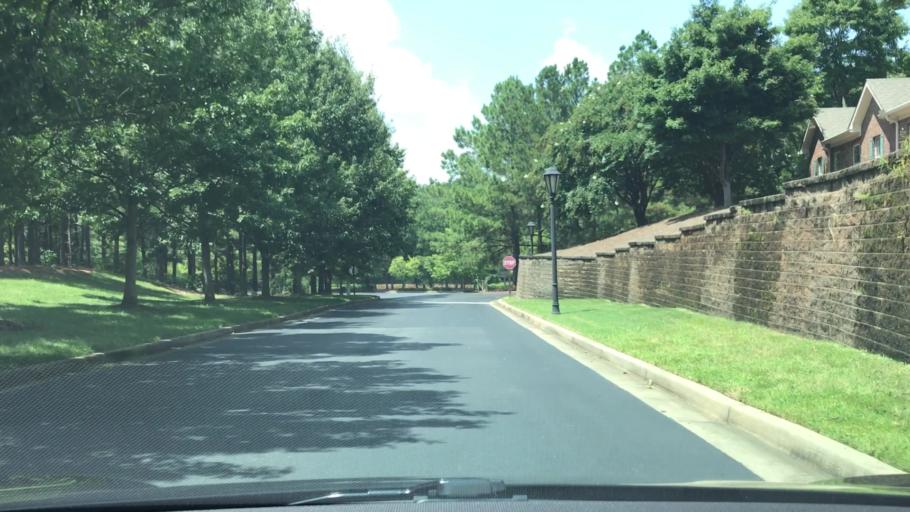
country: US
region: Georgia
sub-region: Fulton County
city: Johns Creek
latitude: 34.0716
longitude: -84.1735
